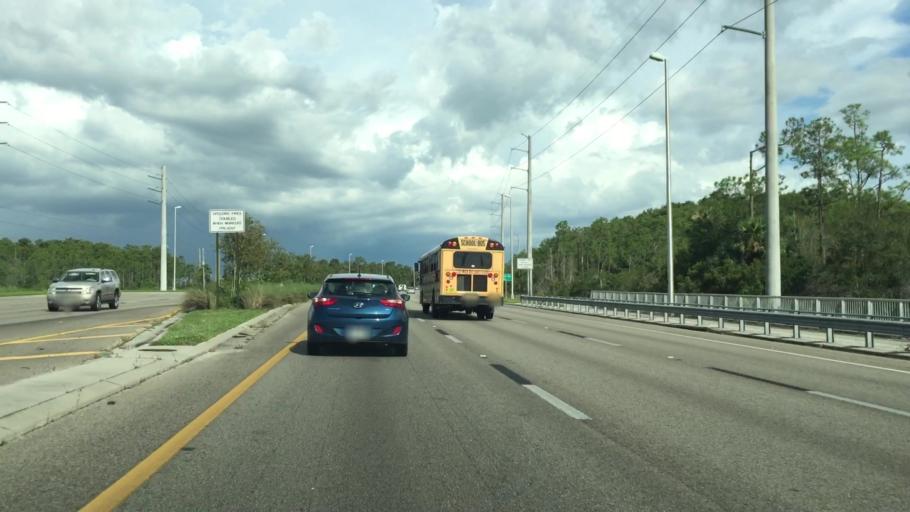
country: US
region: Florida
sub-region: Lee County
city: Tice
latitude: 26.6286
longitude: -81.7804
